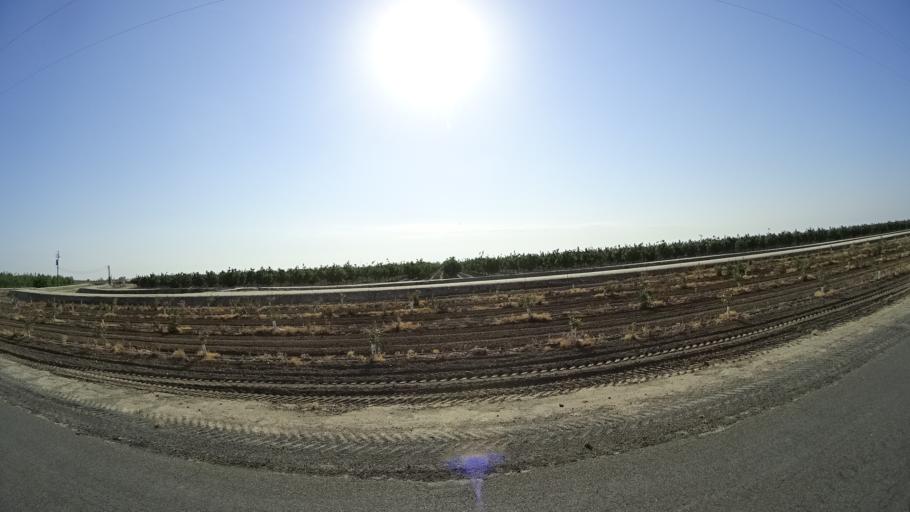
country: US
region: California
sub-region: Kings County
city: Home Garden
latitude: 36.2792
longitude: -119.5652
